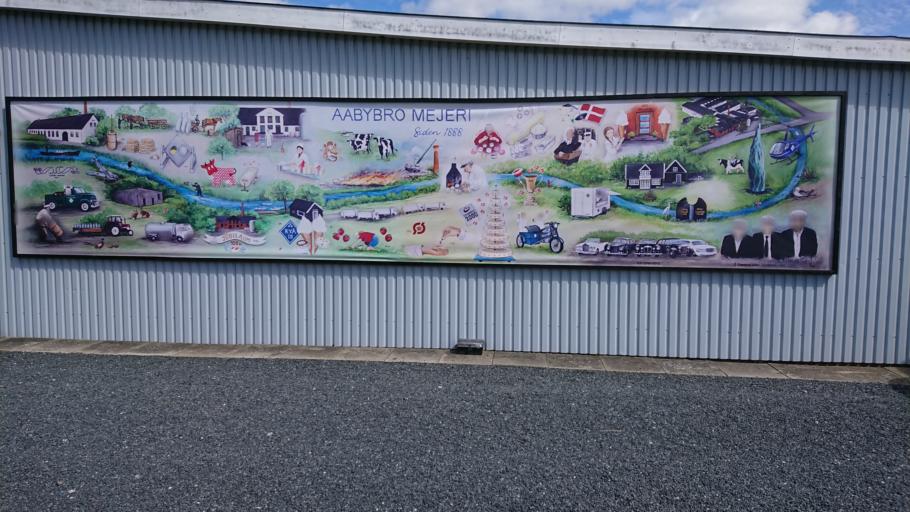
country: DK
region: North Denmark
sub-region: Jammerbugt Kommune
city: Abybro
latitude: 57.1678
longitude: 9.7163
